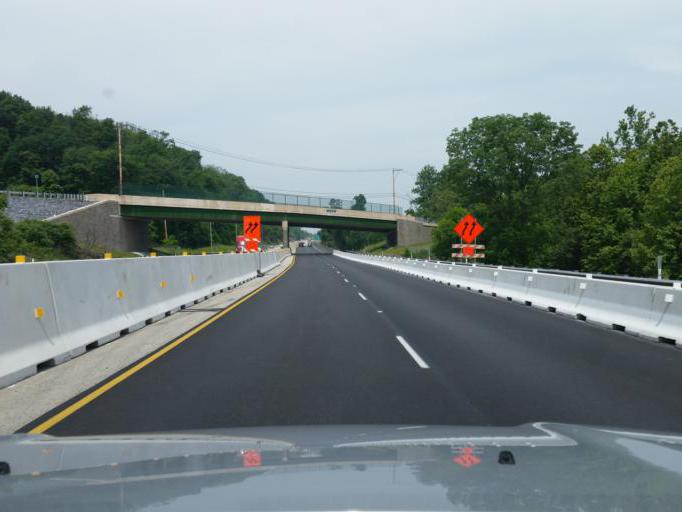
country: US
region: Pennsylvania
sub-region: Dauphin County
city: Steelton
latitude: 40.2047
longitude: -76.8506
